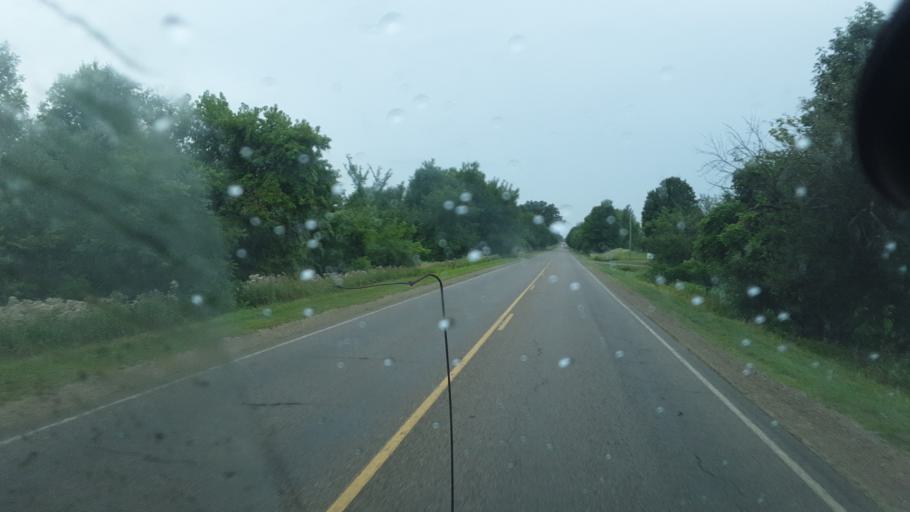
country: US
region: Michigan
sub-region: Hillsdale County
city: Reading
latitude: 41.7078
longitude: -84.7777
